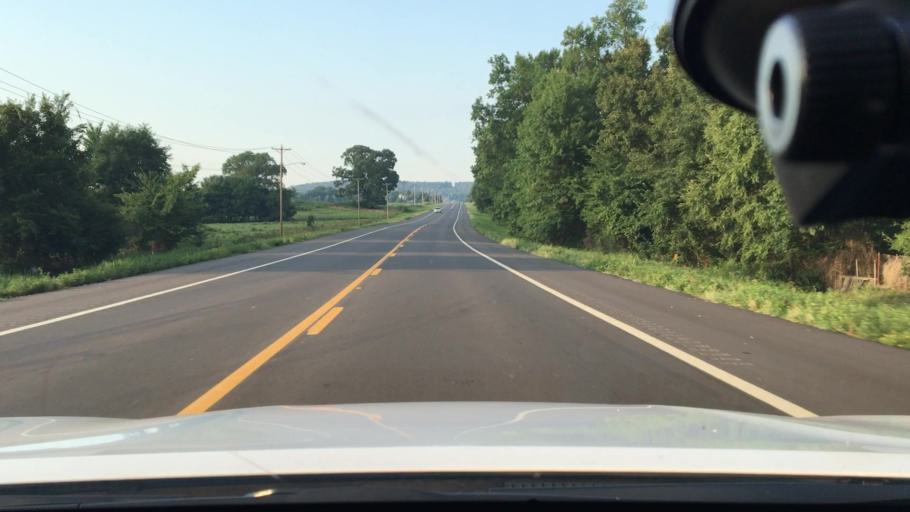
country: US
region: Arkansas
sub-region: Johnson County
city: Clarksville
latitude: 35.4457
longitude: -93.5291
